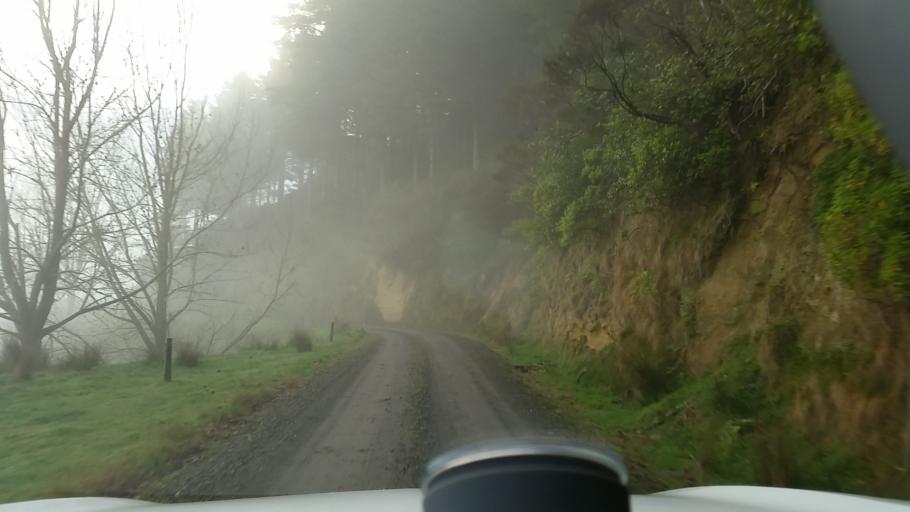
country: NZ
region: Taranaki
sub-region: South Taranaki District
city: Eltham
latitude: -39.4363
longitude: 174.4500
